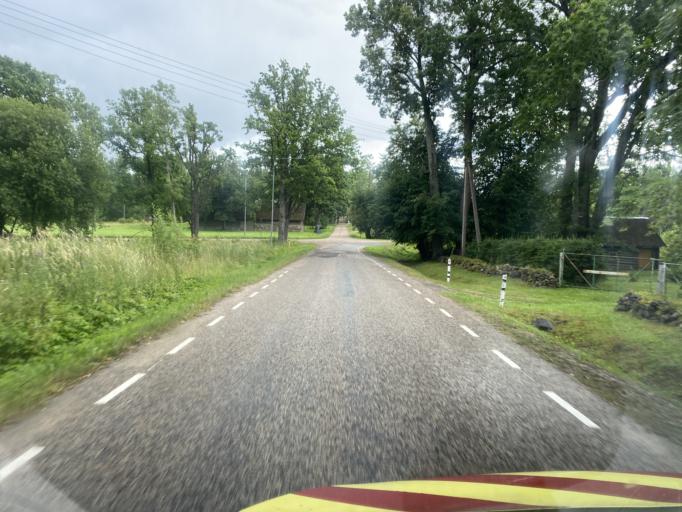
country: EE
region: Valgamaa
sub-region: Torva linn
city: Torva
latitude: 58.0976
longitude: 25.8930
